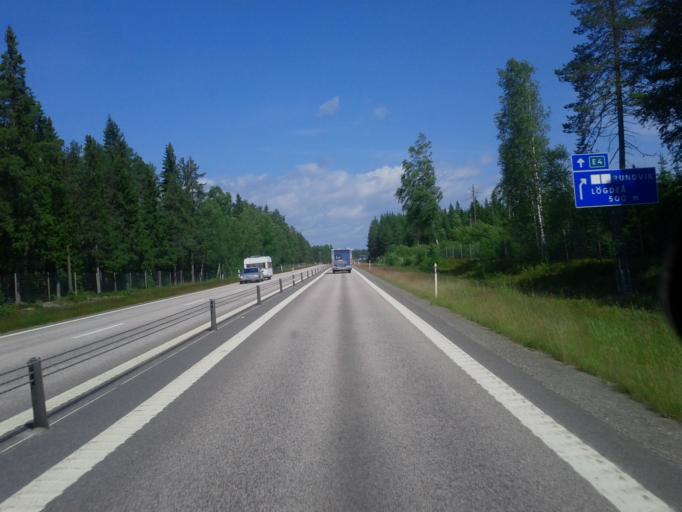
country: SE
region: Vaesterbotten
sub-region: Nordmalings Kommun
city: Nordmaling
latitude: 63.5424
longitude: 19.4077
